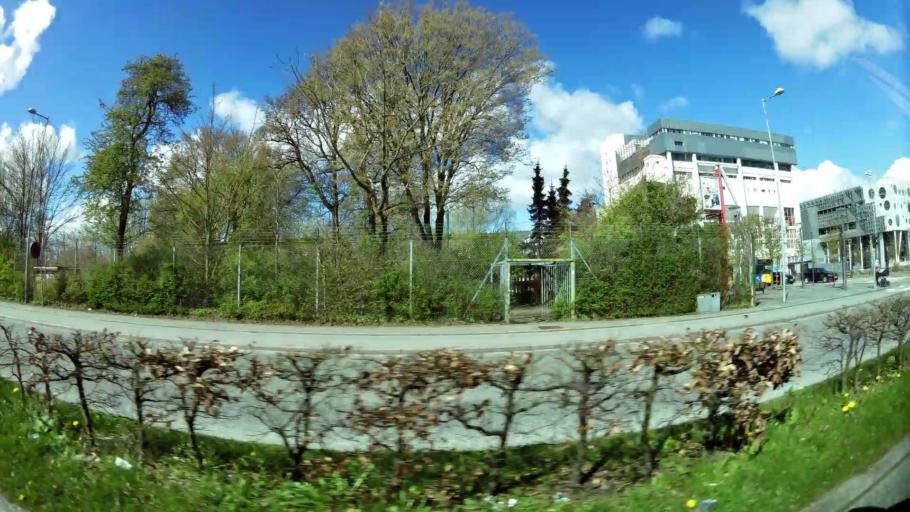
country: DK
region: North Denmark
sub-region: Alborg Kommune
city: Aalborg
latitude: 57.0458
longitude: 9.9343
